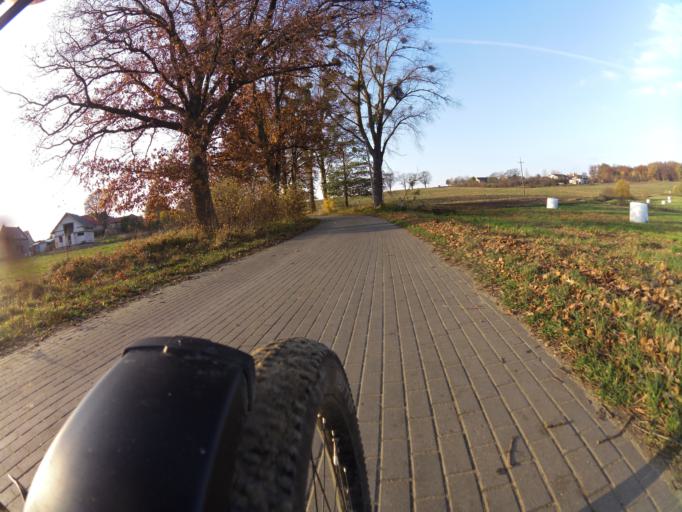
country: PL
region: Pomeranian Voivodeship
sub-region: Powiat pucki
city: Krokowa
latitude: 54.7512
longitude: 18.1881
